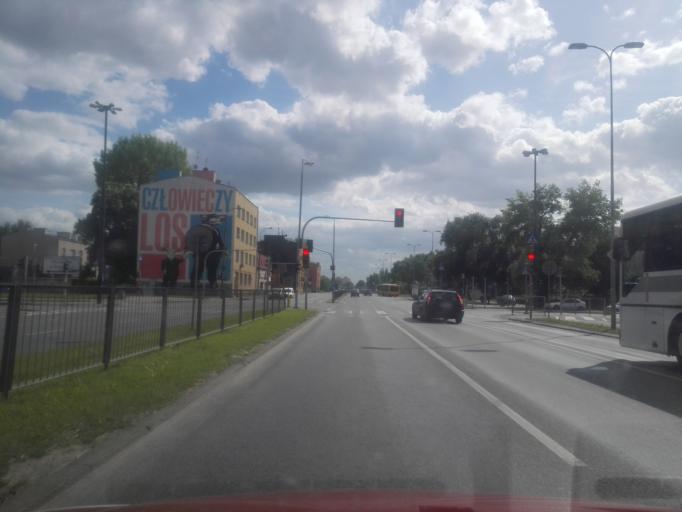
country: PL
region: Masovian Voivodeship
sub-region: Warszawa
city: Targowek
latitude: 52.2733
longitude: 21.0641
